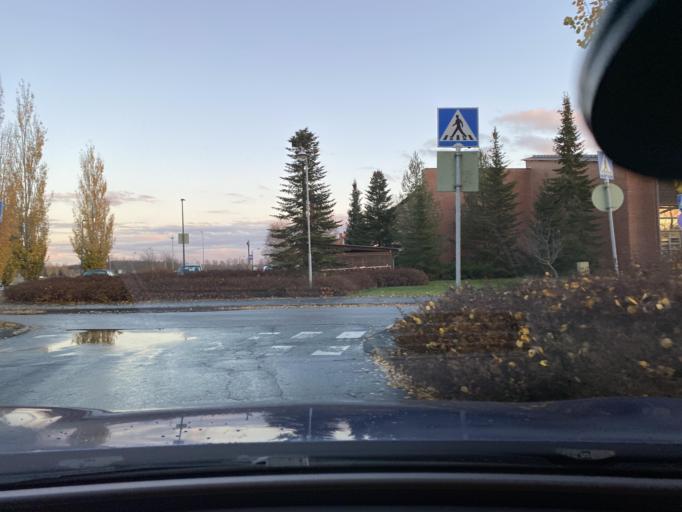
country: FI
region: Satakunta
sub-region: Pori
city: Huittinen
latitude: 61.1838
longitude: 22.6969
